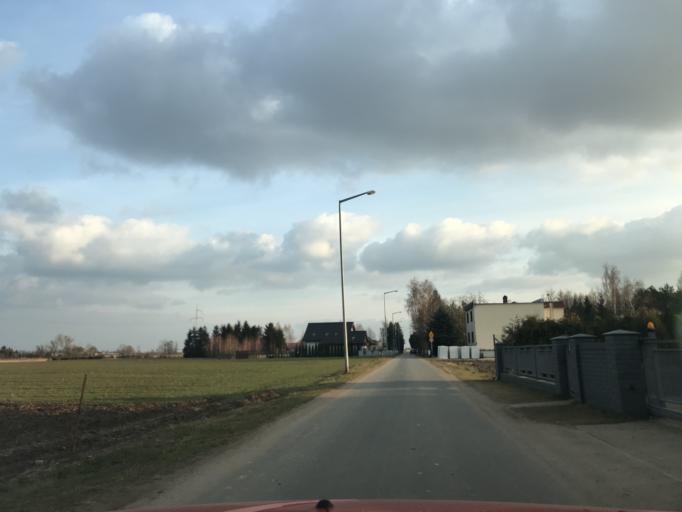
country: PL
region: Greater Poland Voivodeship
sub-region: Powiat poznanski
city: Tarnowo Podgorne
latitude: 52.4396
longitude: 16.7213
